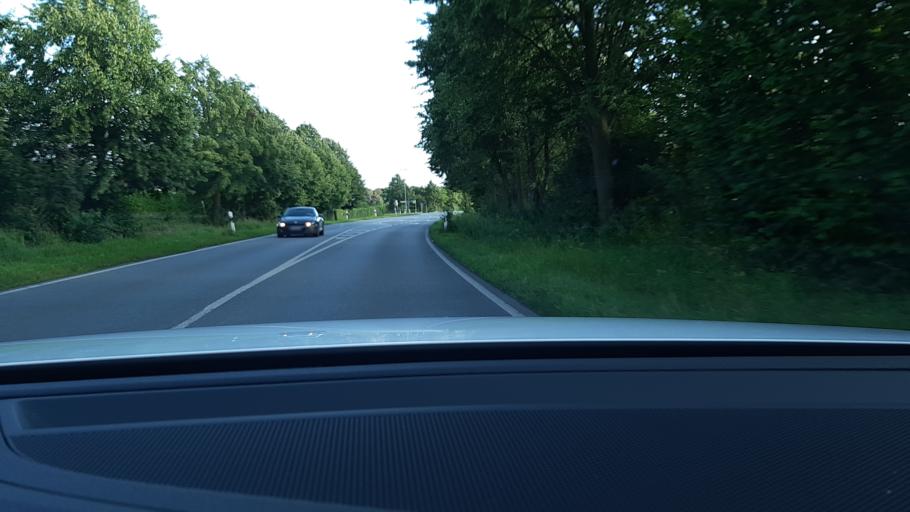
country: DE
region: Schleswig-Holstein
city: Stockelsdorf
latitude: 53.9067
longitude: 10.6406
